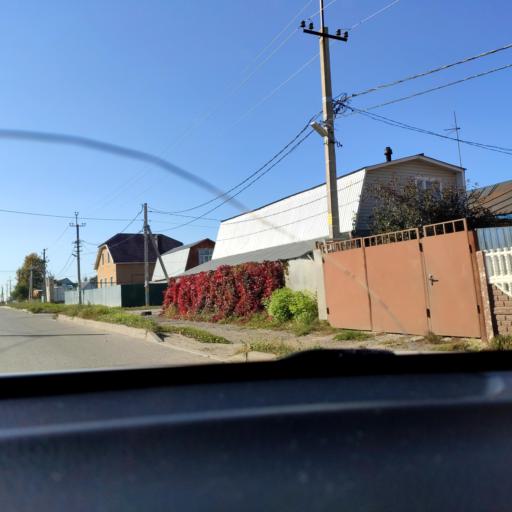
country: RU
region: Tatarstan
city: Vysokaya Gora
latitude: 55.8505
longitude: 49.2319
